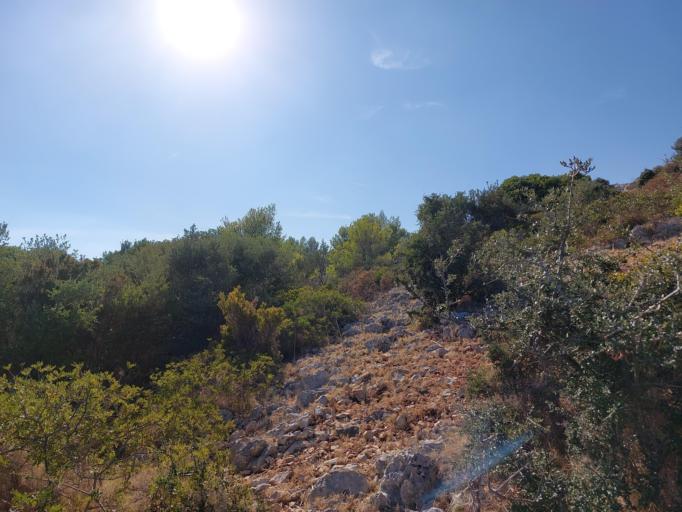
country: HR
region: Dubrovacko-Neretvanska
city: Smokvica
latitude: 42.7332
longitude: 16.8404
